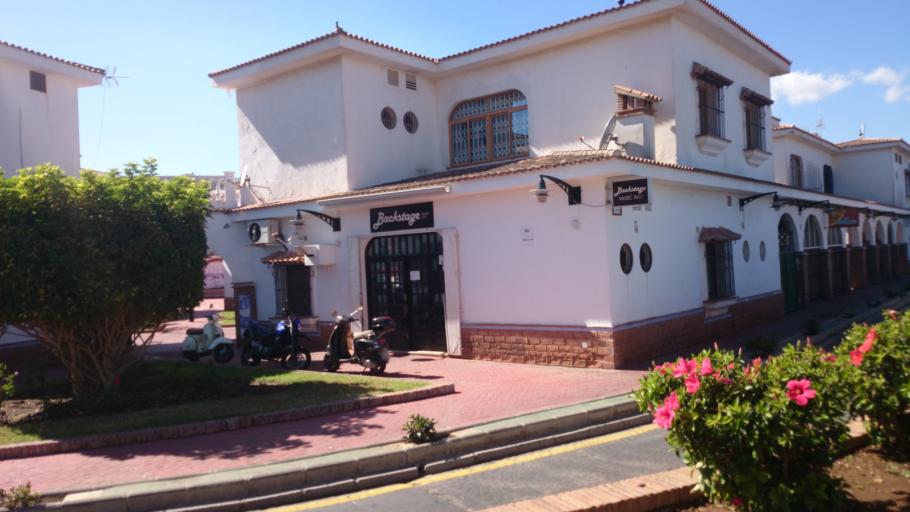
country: ES
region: Ceuta
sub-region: Ceuta
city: Ceuta
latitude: 35.8897
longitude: -5.3119
